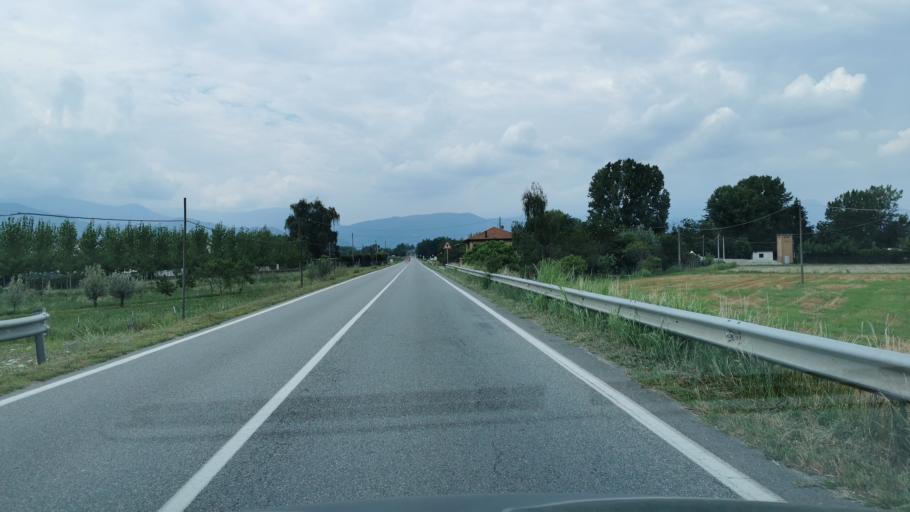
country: IT
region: Piedmont
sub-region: Provincia di Torino
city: Garzigliana
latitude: 44.8311
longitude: 7.3663
